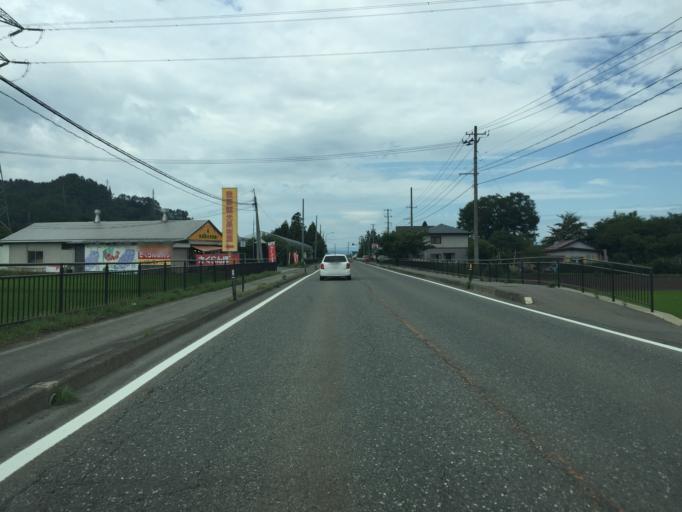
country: JP
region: Yamagata
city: Yonezawa
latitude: 37.8881
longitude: 140.1792
